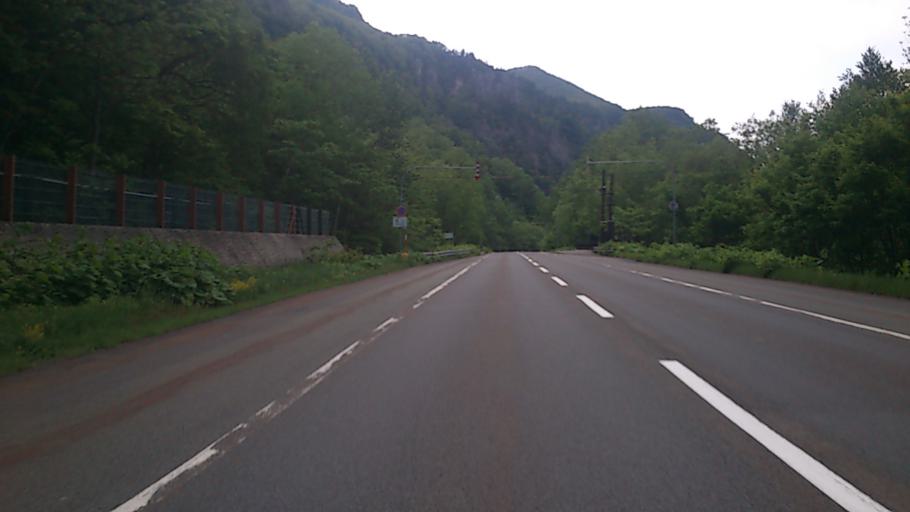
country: JP
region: Hokkaido
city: Kamikawa
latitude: 43.7550
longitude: 142.9275
